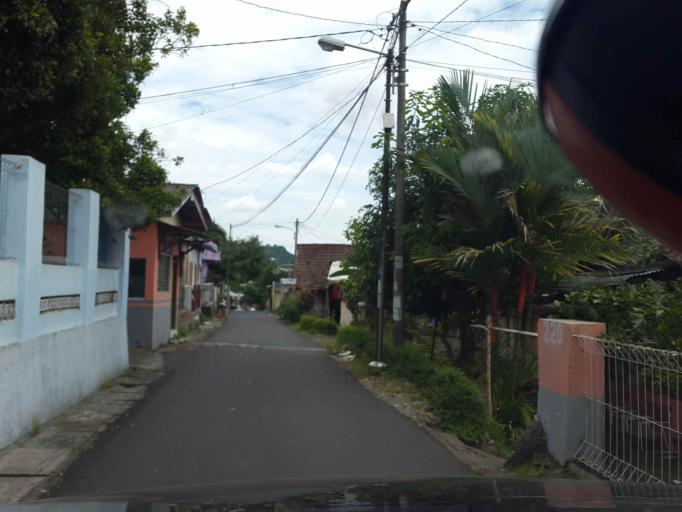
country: ID
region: Central Java
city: Salatiga
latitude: -7.3191
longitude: 110.5028
